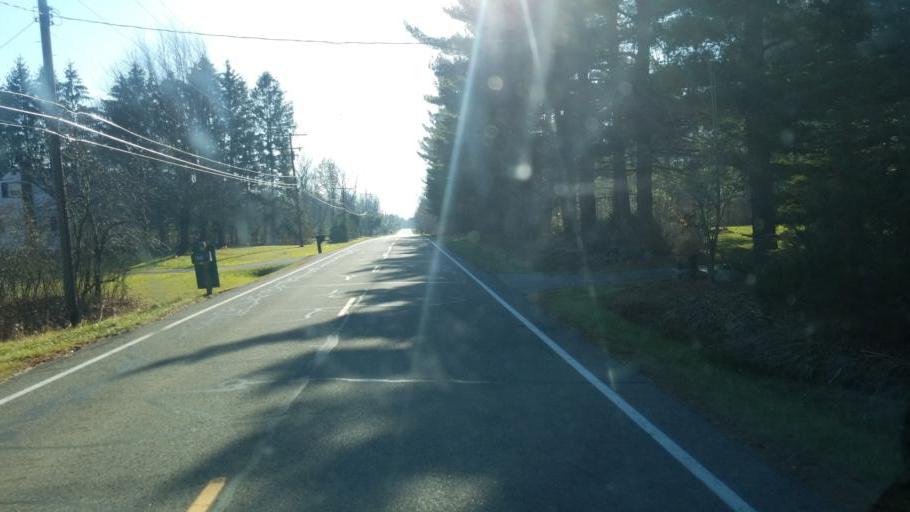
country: US
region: Ohio
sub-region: Geauga County
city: Burton
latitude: 41.4447
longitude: -81.2455
